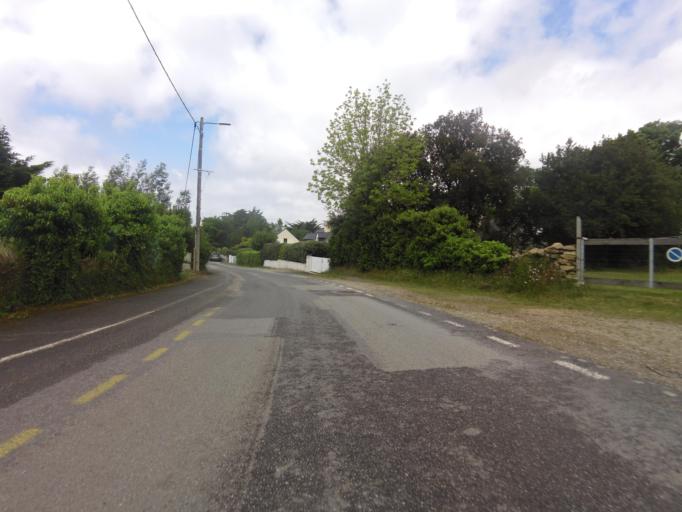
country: FR
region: Brittany
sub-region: Departement du Morbihan
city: Larmor-Baden
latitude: 47.5871
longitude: -2.8933
